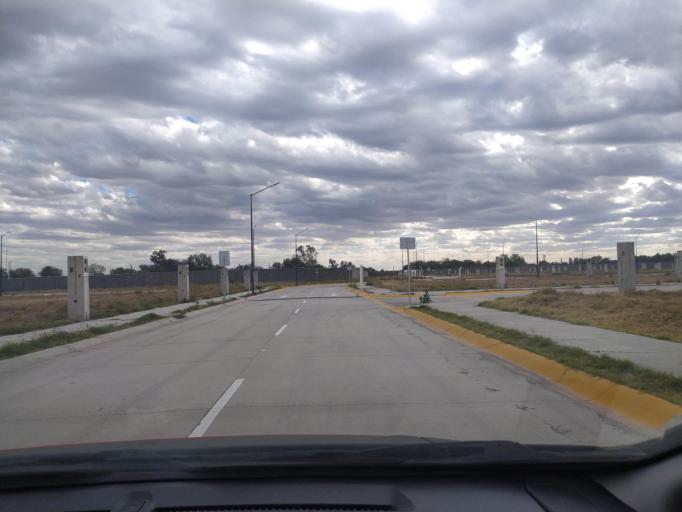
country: LA
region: Oudomxai
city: Muang La
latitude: 21.0250
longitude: 101.8220
